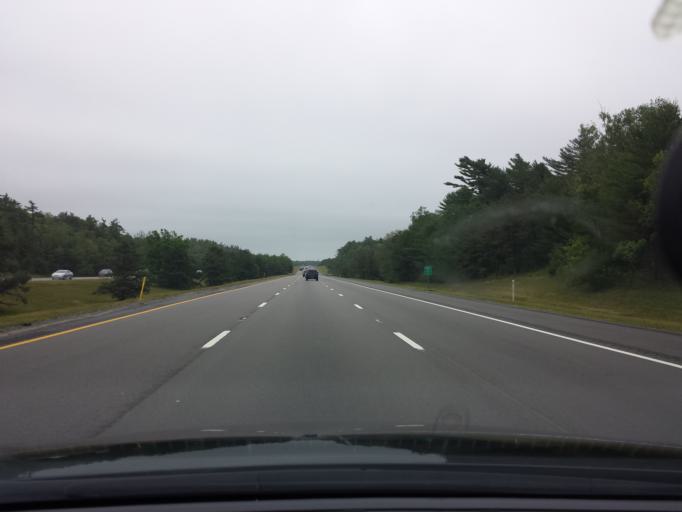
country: US
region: Massachusetts
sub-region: Plymouth County
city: White Island Shores
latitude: 41.7754
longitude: -70.6341
